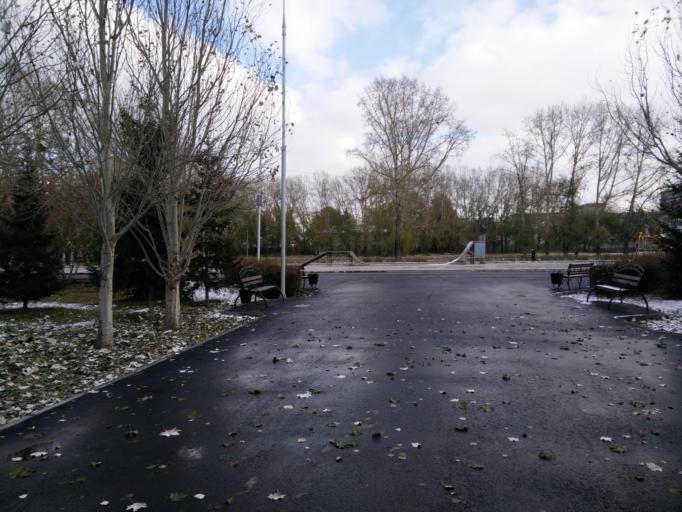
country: RU
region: Novosibirsk
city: Berdsk
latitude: 54.7570
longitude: 83.1049
